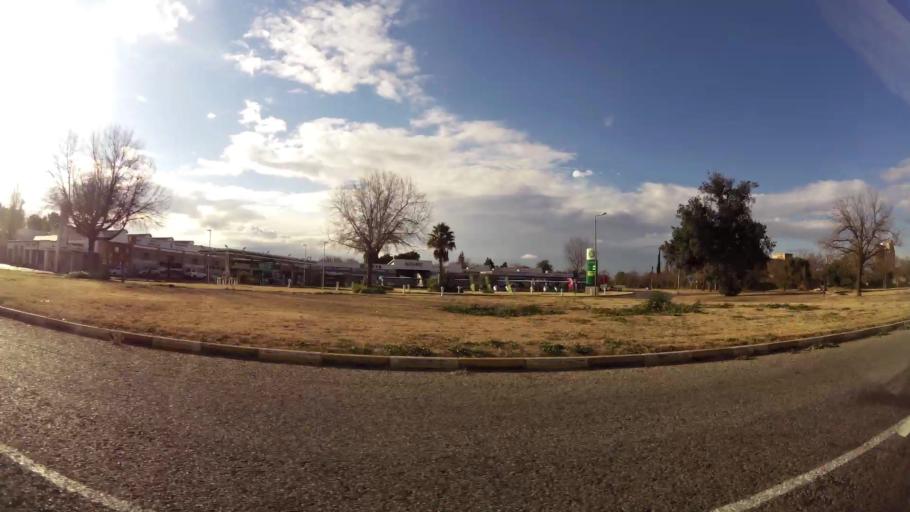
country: ZA
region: Orange Free State
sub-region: Lejweleputswa District Municipality
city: Welkom
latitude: -27.9866
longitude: 26.7254
